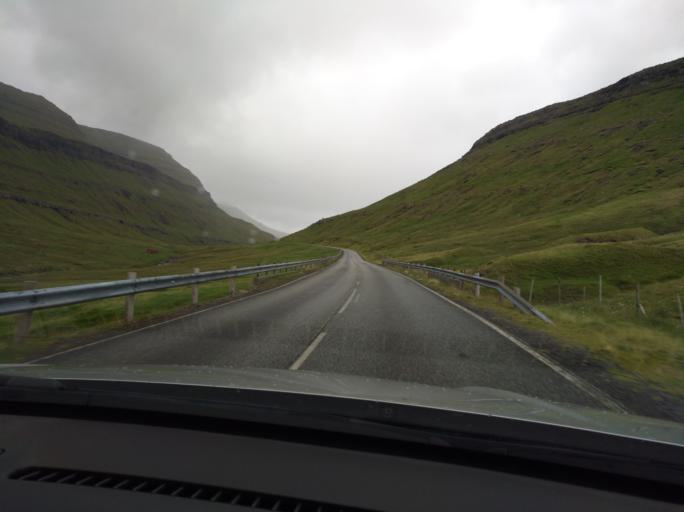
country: FO
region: Eysturoy
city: Fuglafjordur
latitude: 62.2266
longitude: -6.8793
